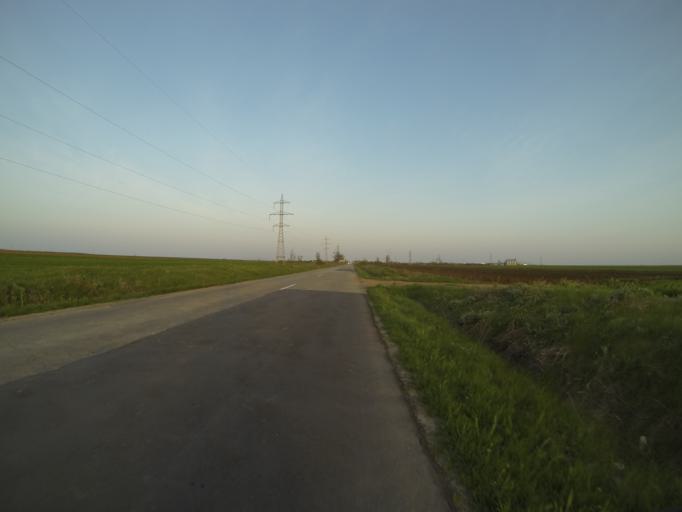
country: RO
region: Dolj
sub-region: Comuna Dranicu
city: Dranic
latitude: 44.0612
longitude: 23.8228
